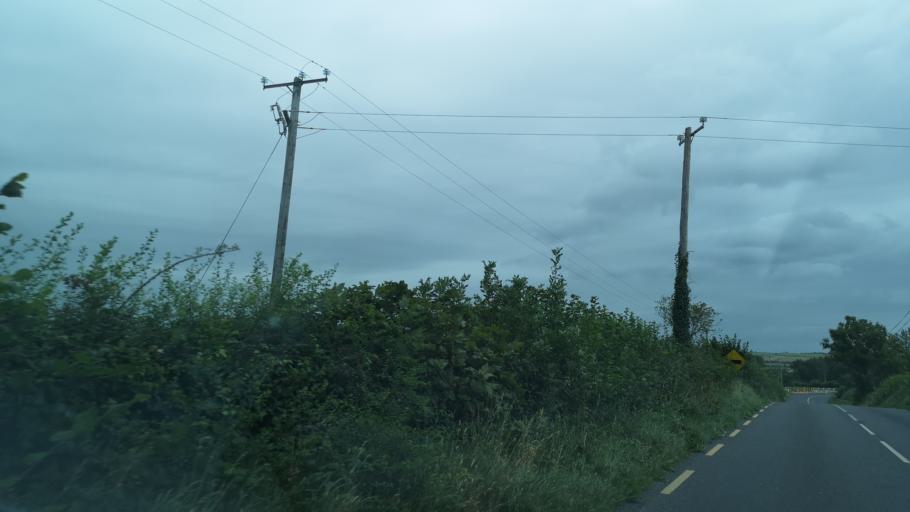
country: IE
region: Leinster
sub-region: Uibh Fhaili
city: Banagher
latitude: 53.2090
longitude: -7.9112
